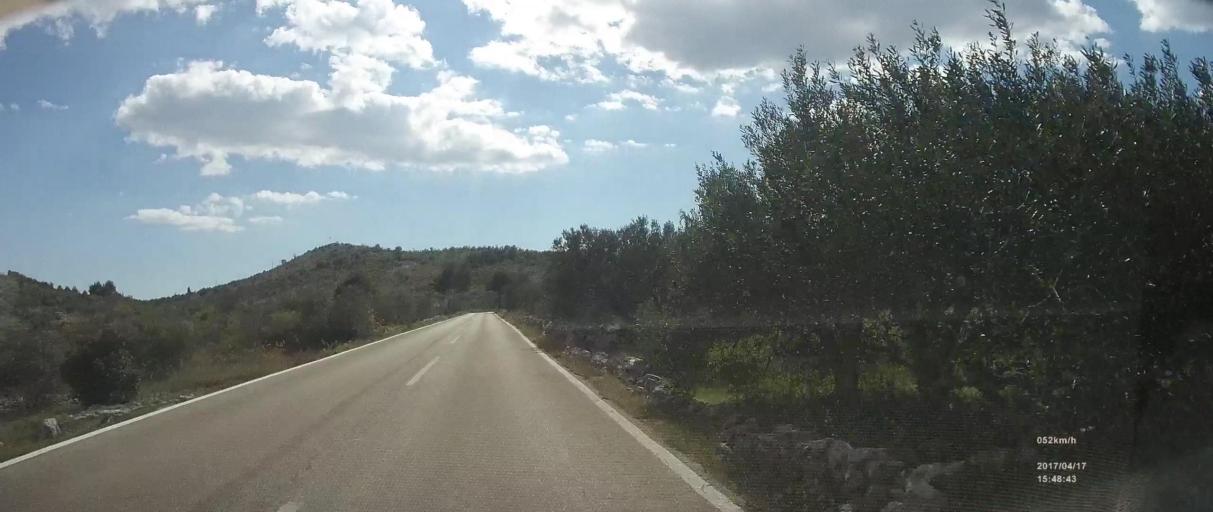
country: HR
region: Sibensko-Kniniska
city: Primosten
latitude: 43.6194
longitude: 15.9789
